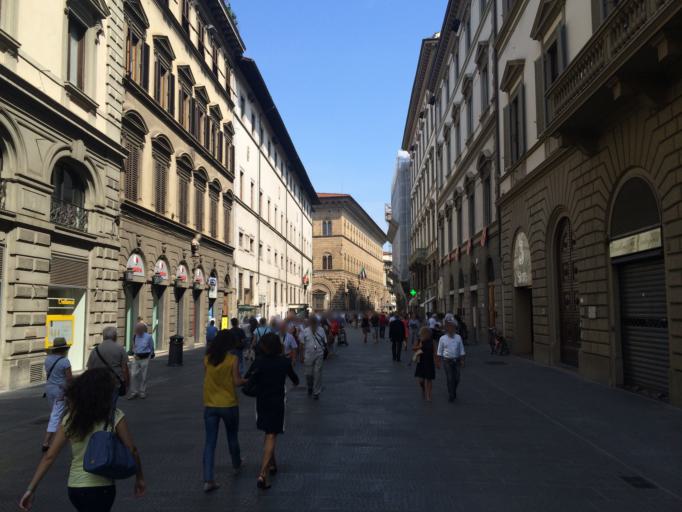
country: IT
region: Tuscany
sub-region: Province of Florence
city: Florence
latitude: 43.7738
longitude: 11.2554
